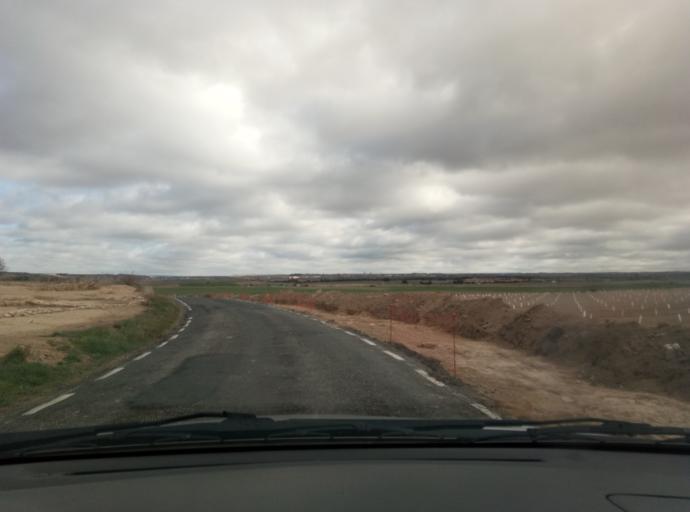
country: ES
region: Catalonia
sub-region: Provincia de Lleida
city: Verdu
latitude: 41.5964
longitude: 1.0964
